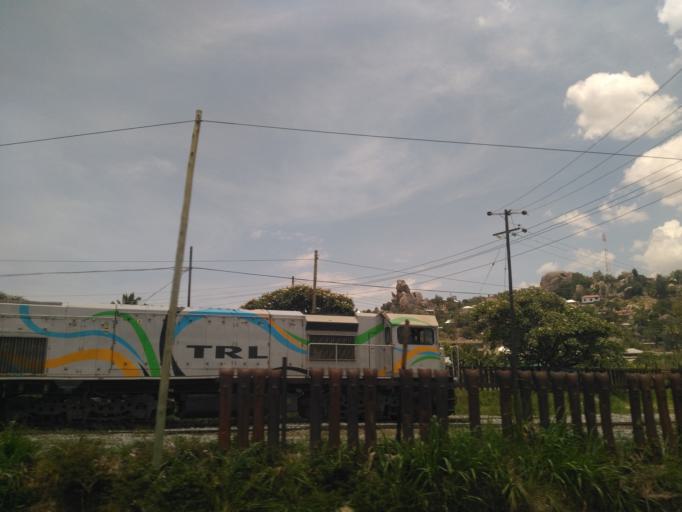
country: TZ
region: Mwanza
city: Mwanza
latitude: -2.5442
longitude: 32.9051
